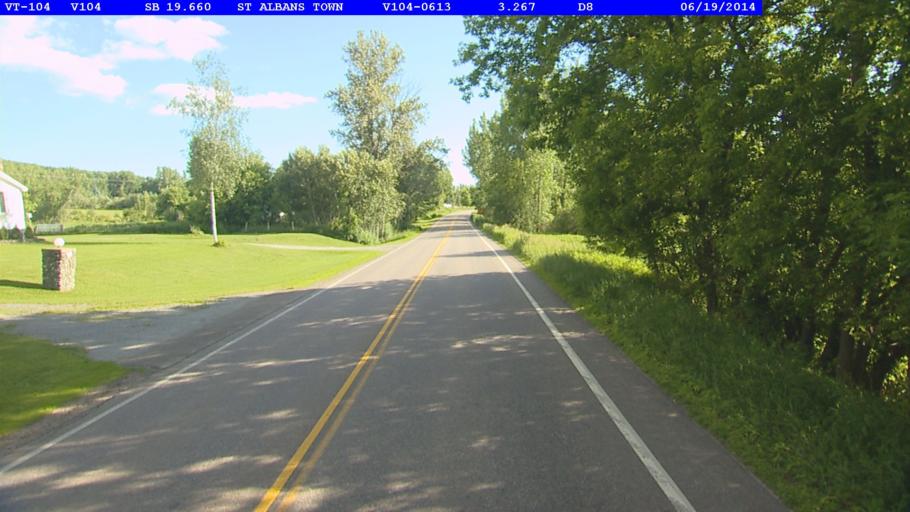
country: US
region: Vermont
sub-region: Franklin County
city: Saint Albans
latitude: 44.8175
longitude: -73.0596
